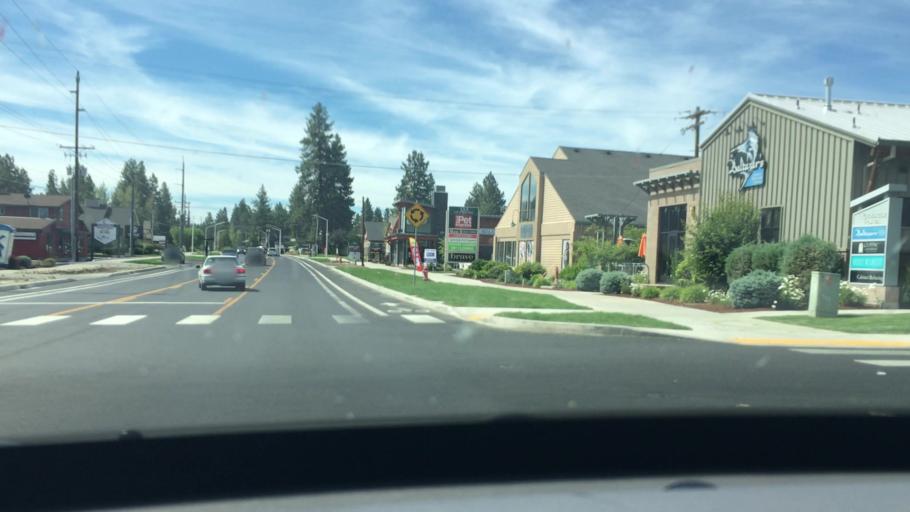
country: US
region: Oregon
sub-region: Deschutes County
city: Bend
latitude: 44.0505
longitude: -121.3319
